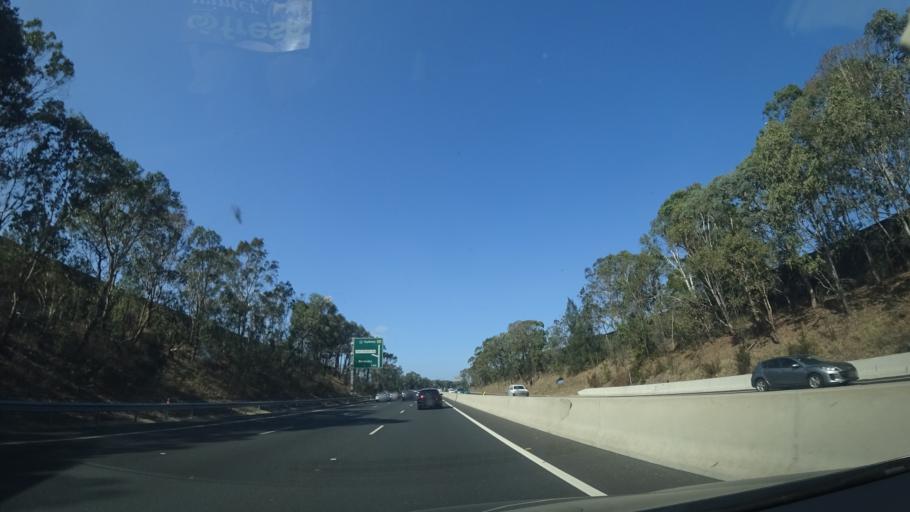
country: AU
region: New South Wales
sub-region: Bankstown
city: Revesby
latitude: -33.9420
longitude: 151.0020
